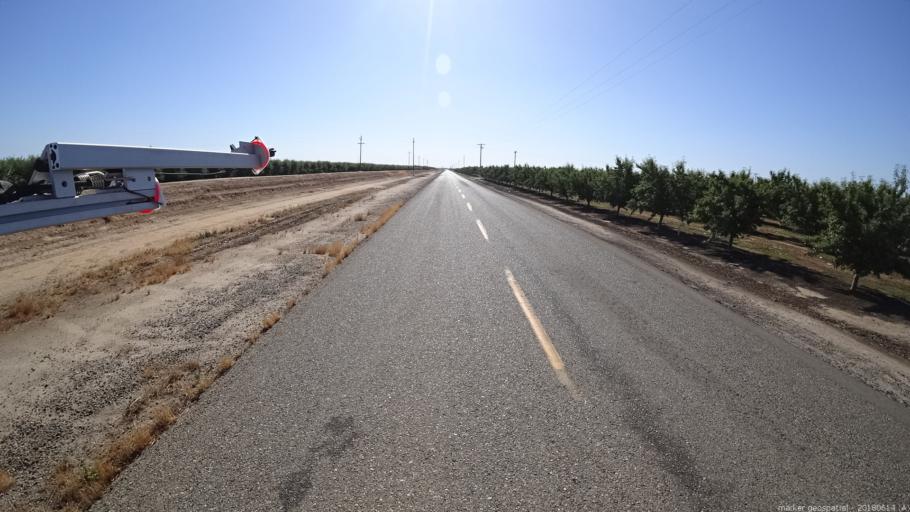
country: US
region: California
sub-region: Madera County
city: Madera Acres
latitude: 36.9820
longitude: -120.1440
